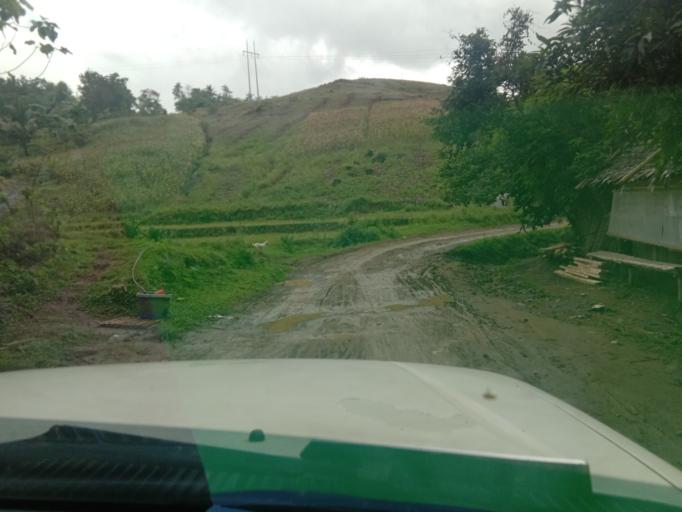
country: PH
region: Western Visayas
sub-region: Province of Capiz
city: Lantangan
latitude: 11.3713
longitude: 122.8853
